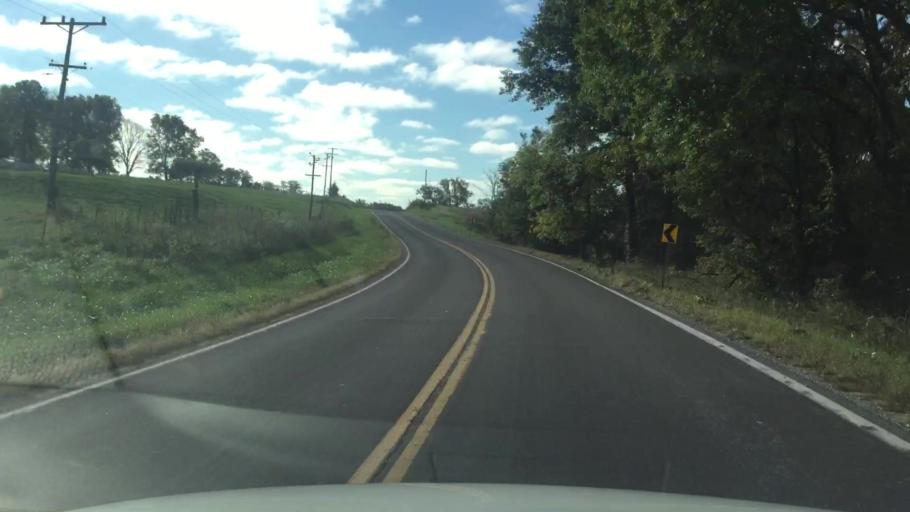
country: US
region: Missouri
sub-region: Howard County
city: New Franklin
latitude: 39.0637
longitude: -92.7460
